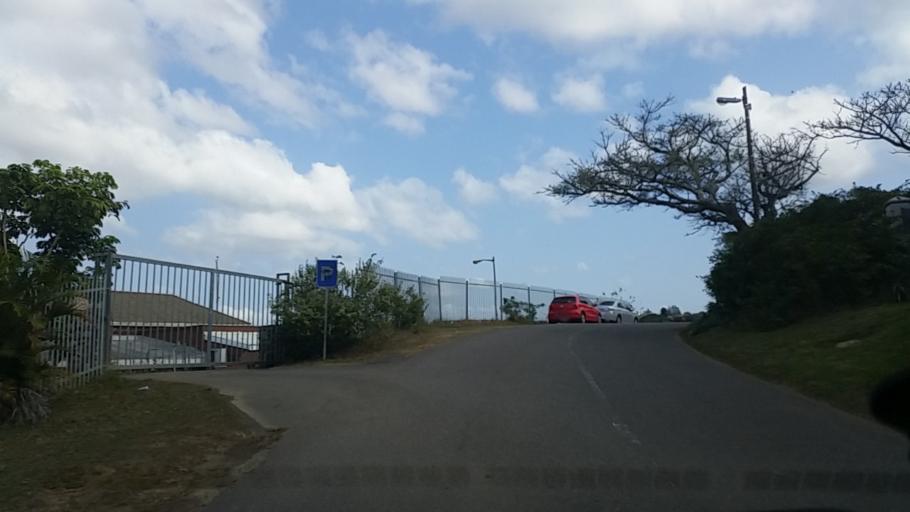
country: ZA
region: KwaZulu-Natal
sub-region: eThekwini Metropolitan Municipality
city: Berea
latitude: -29.8314
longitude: 30.9526
